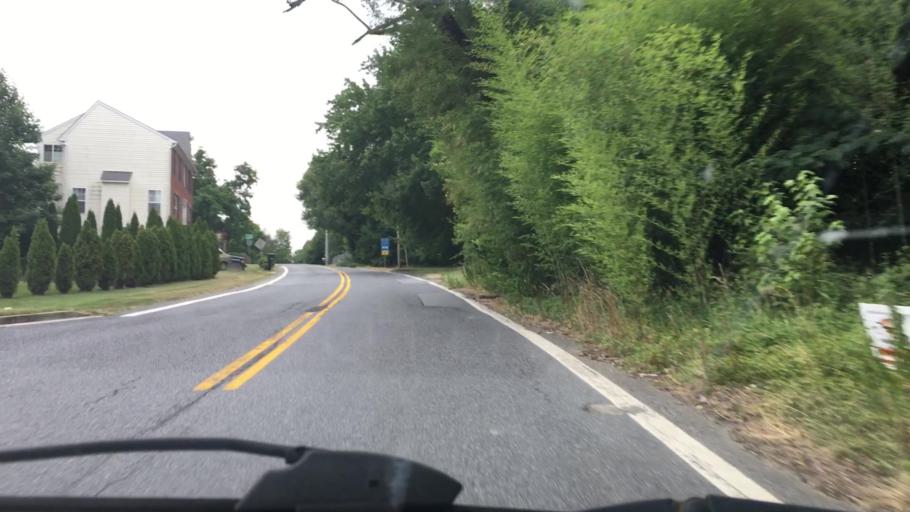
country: US
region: Maryland
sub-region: Prince George's County
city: Glenn Dale
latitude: 39.0131
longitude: -76.7818
